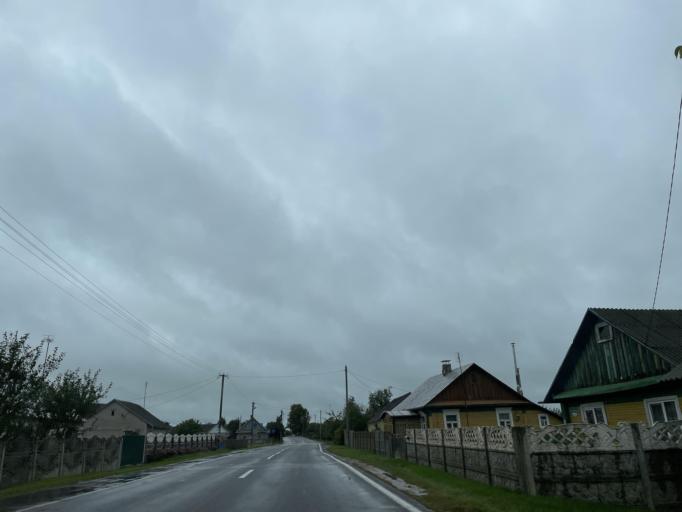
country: BY
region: Minsk
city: Snow
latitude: 53.2125
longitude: 26.3718
